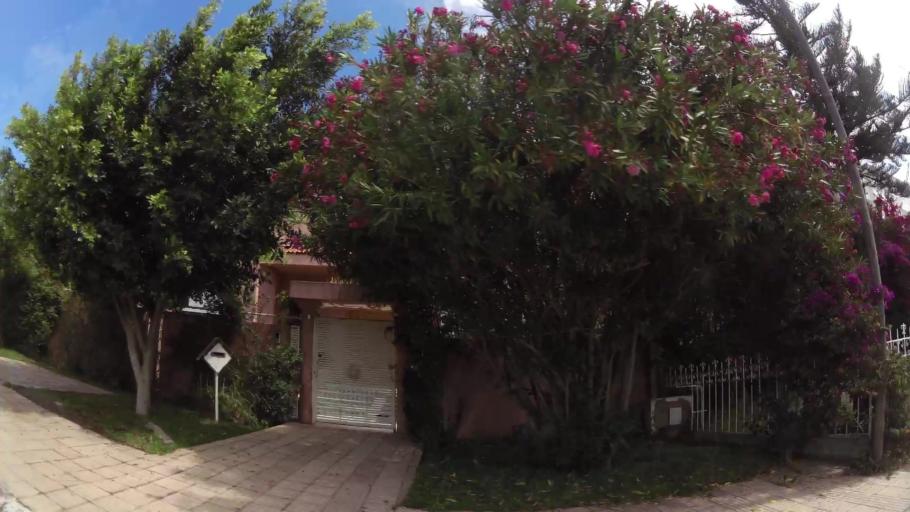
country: MA
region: Gharb-Chrarda-Beni Hssen
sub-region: Kenitra Province
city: Kenitra
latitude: 34.2415
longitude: -6.6058
